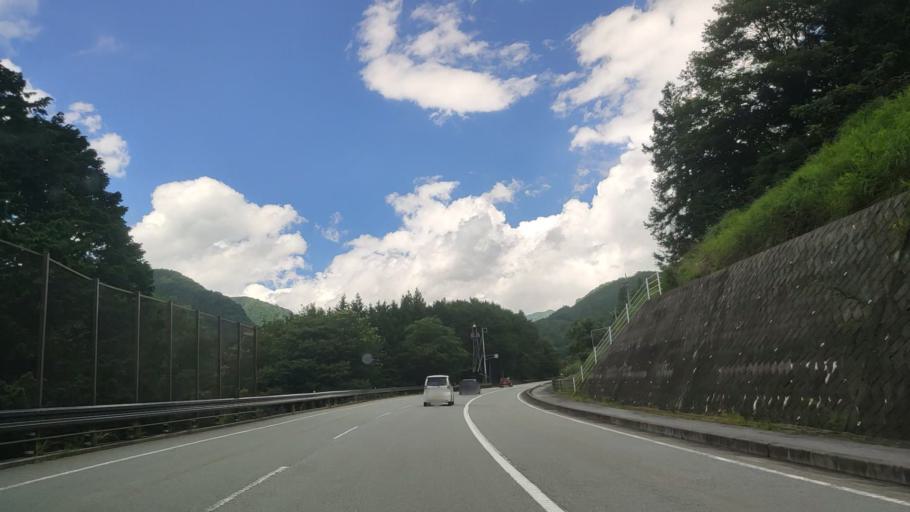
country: JP
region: Yamanashi
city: Enzan
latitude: 35.8116
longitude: 138.7521
